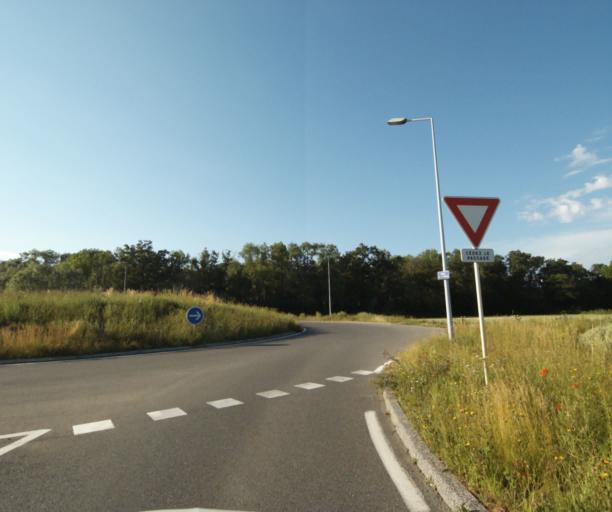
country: FR
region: Rhone-Alpes
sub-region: Departement de la Haute-Savoie
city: Allinges
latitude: 46.3544
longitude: 6.4532
